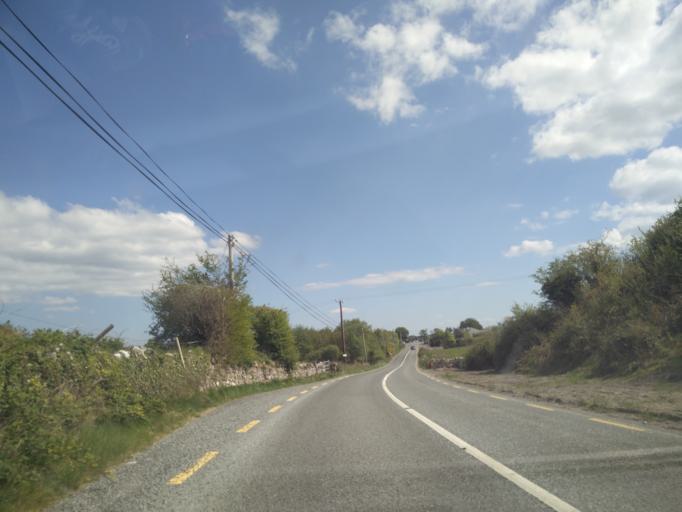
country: IE
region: Connaught
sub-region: Maigh Eo
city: Westport
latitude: 53.7841
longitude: -9.4493
